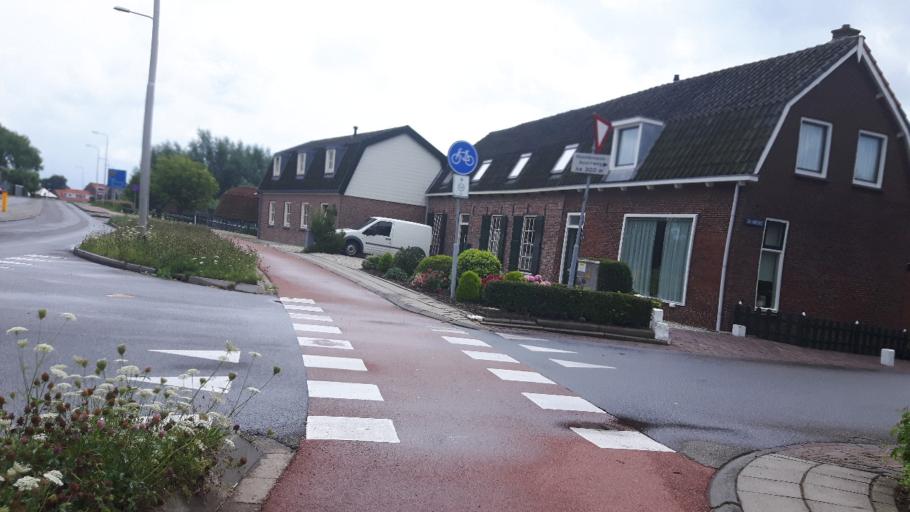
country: NL
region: Utrecht
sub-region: Gemeente Oudewater
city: Oudewater
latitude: 52.0170
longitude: 4.8739
